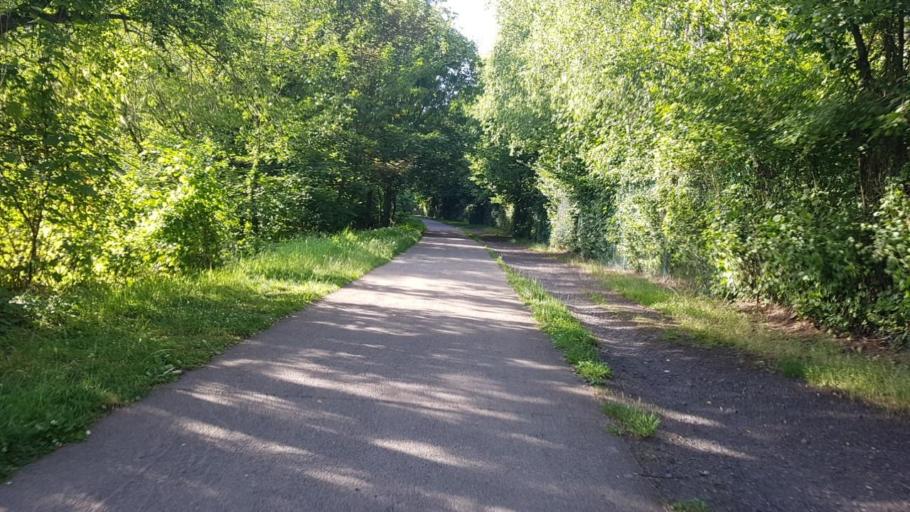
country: BE
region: Wallonia
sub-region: Province de Liege
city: Chaudfontaine
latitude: 50.6147
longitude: 5.6250
